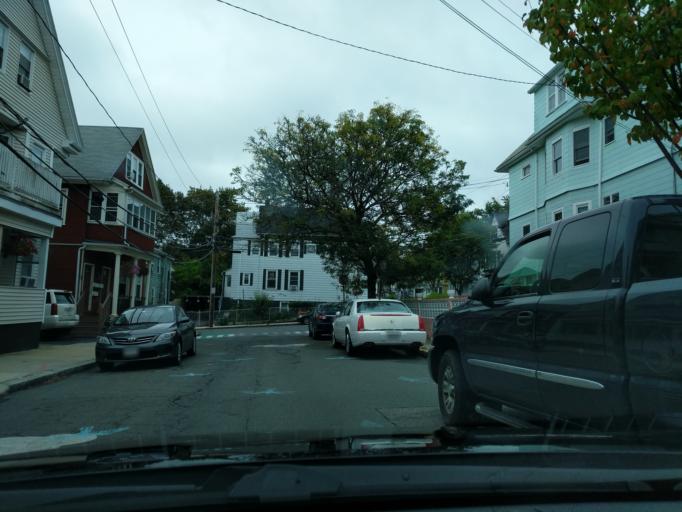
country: US
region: Massachusetts
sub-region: Middlesex County
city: Somerville
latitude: 42.3895
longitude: -71.1013
